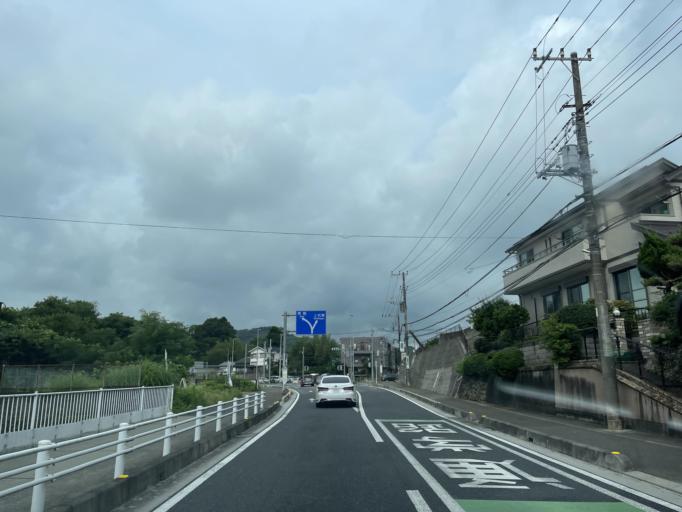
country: JP
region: Saitama
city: Hanno
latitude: 35.8588
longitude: 139.3063
